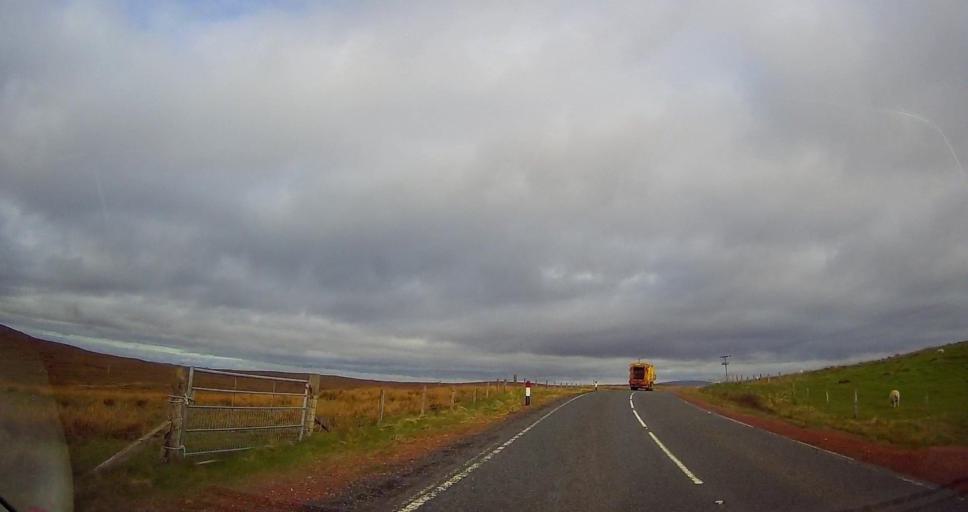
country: GB
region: Scotland
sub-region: Shetland Islands
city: Lerwick
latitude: 60.4470
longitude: -1.2075
